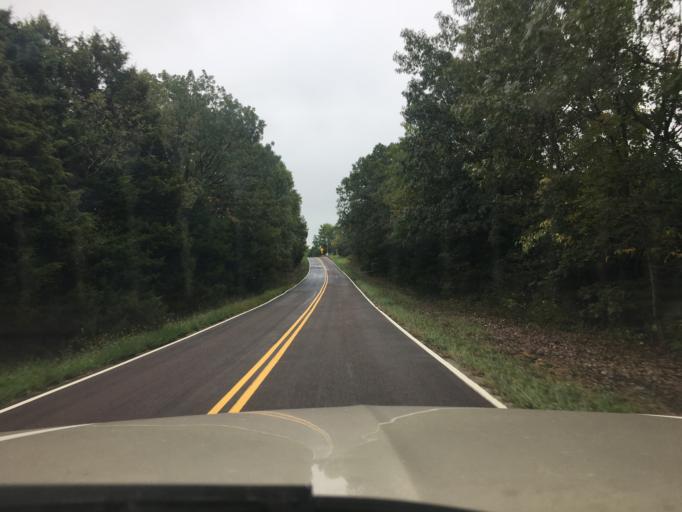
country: US
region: Missouri
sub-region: Crawford County
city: Cuba
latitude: 38.1915
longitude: -91.4764
